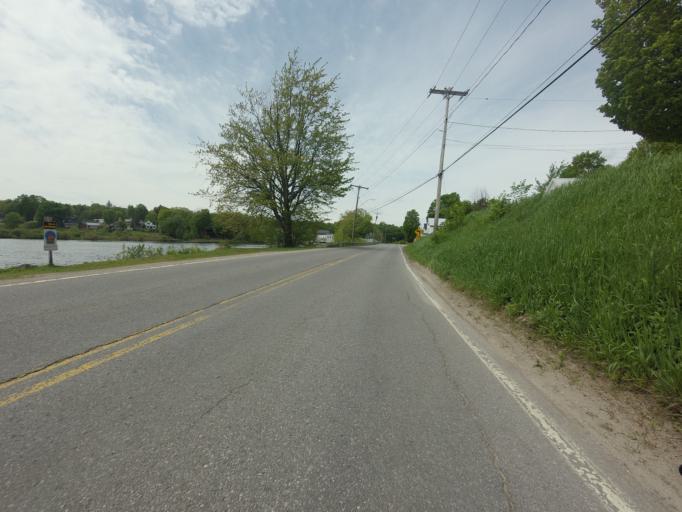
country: US
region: New York
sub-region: St. Lawrence County
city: Hannawa Falls
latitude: 44.5539
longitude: -74.9346
